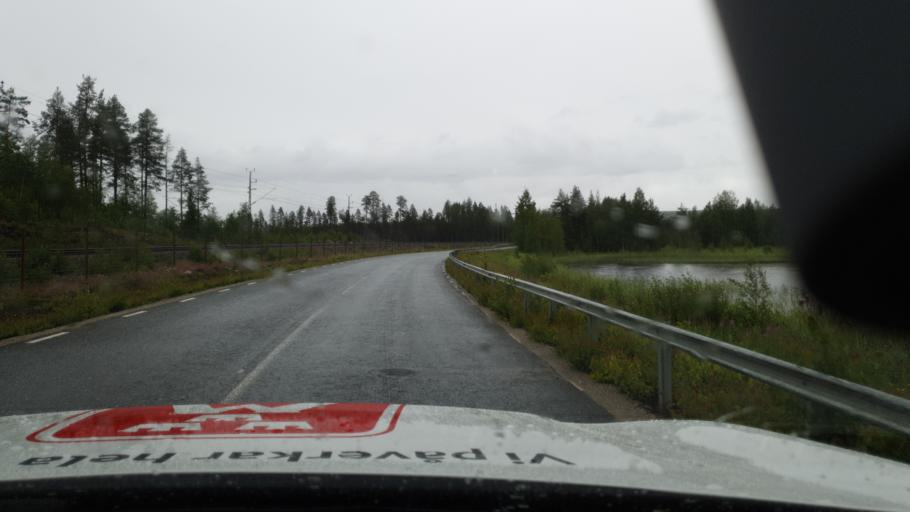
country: SE
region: Vaesterbotten
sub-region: Vindelns Kommun
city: Vindeln
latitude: 64.4526
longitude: 19.7469
